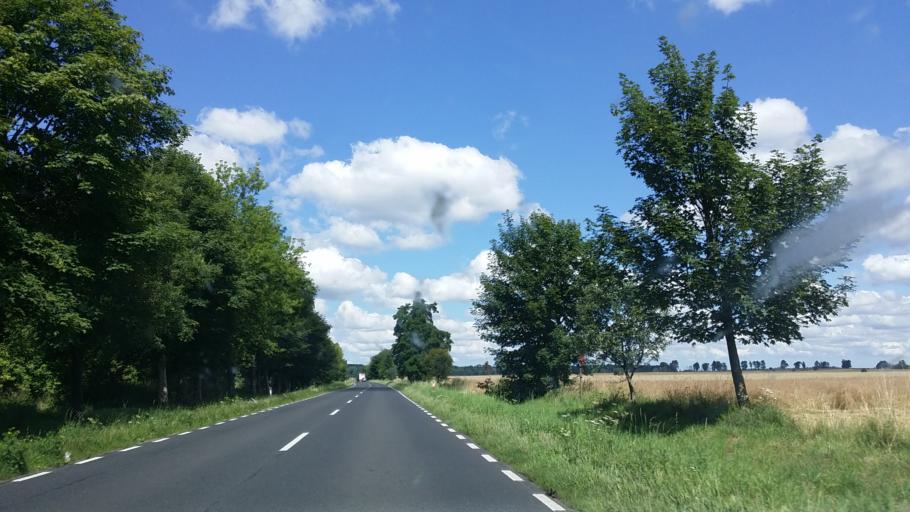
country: PL
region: West Pomeranian Voivodeship
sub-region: Powiat swidwinski
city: Swidwin
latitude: 53.8183
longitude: 15.7586
